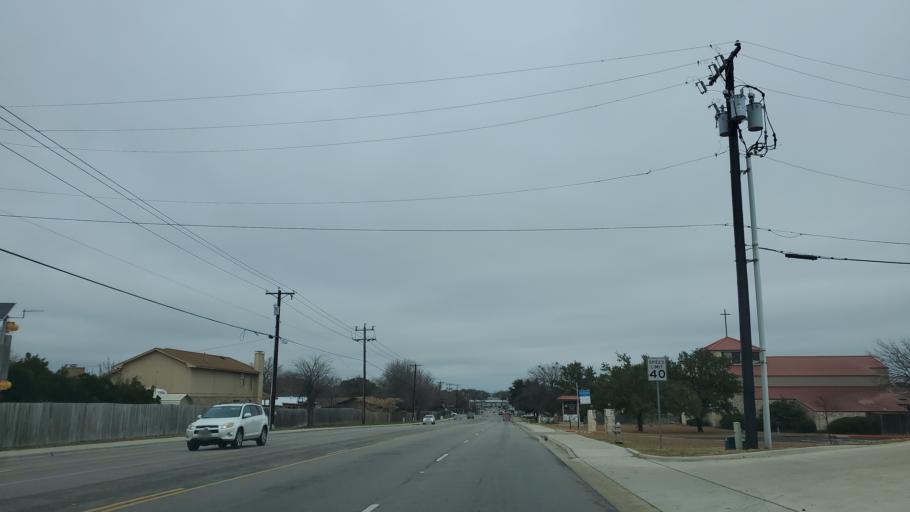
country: US
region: Texas
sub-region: Bell County
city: Killeen
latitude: 31.0862
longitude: -97.7356
